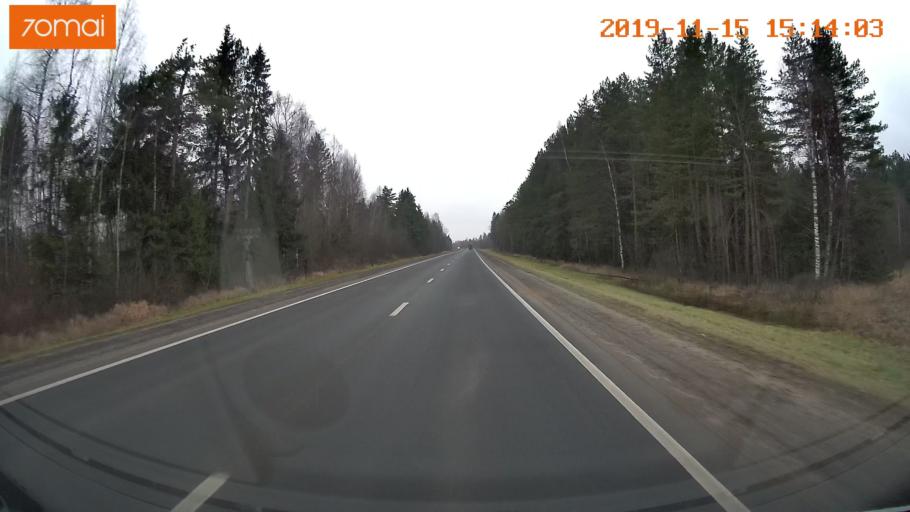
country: RU
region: Jaroslavl
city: Danilov
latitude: 58.3053
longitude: 40.2103
